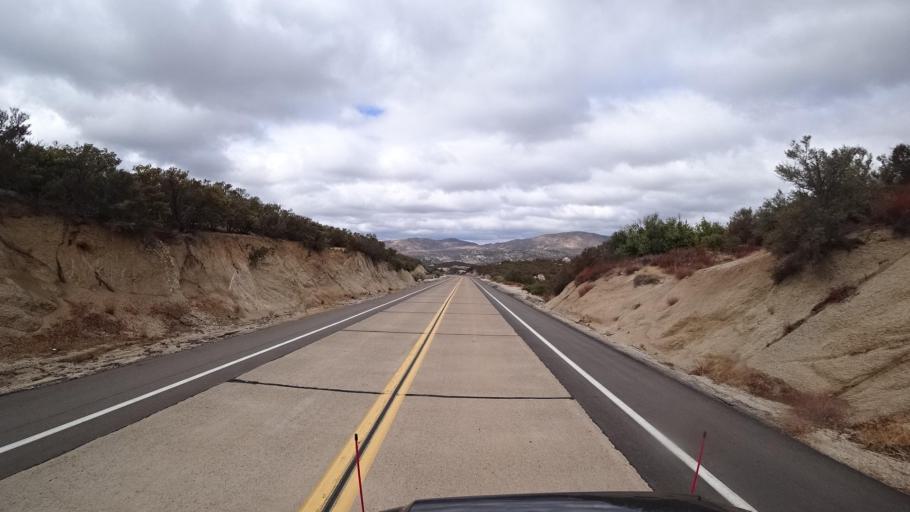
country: US
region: California
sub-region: San Diego County
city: Campo
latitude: 32.7214
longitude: -116.4090
